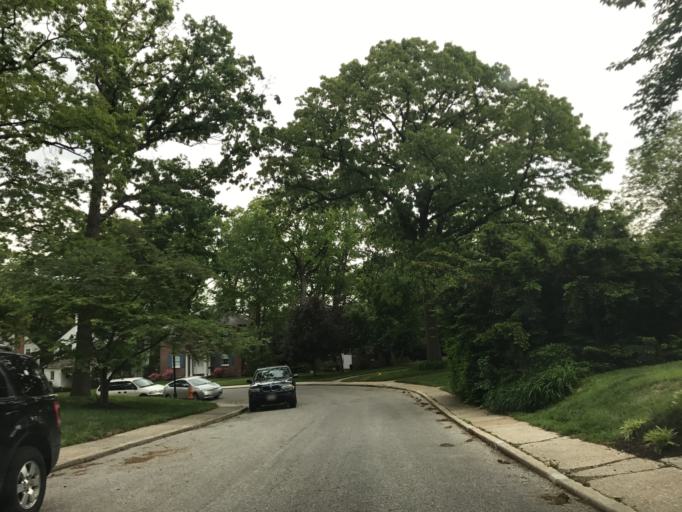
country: US
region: Maryland
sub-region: City of Baltimore
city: Baltimore
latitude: 39.3405
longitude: -76.5966
